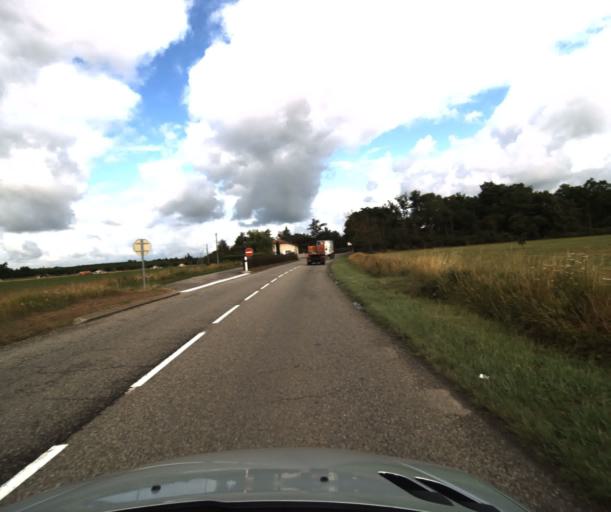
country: FR
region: Midi-Pyrenees
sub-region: Departement du Tarn-et-Garonne
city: Castelsarrasin
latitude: 44.0265
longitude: 1.0589
